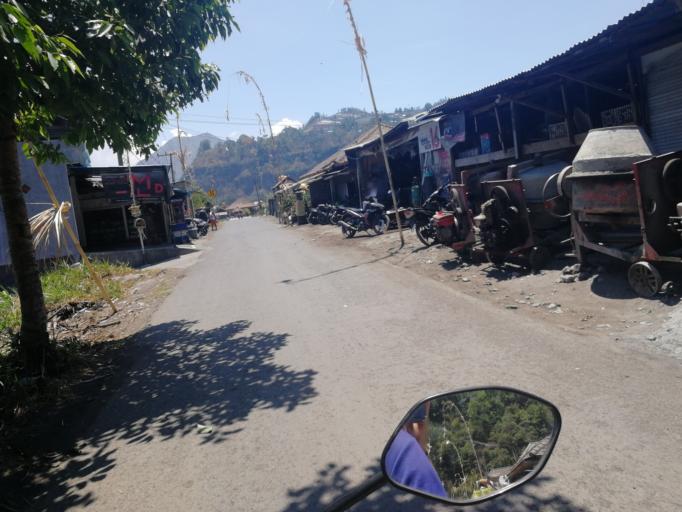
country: ID
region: Bali
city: Banjar Trunyan
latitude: -8.2216
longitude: 115.4167
